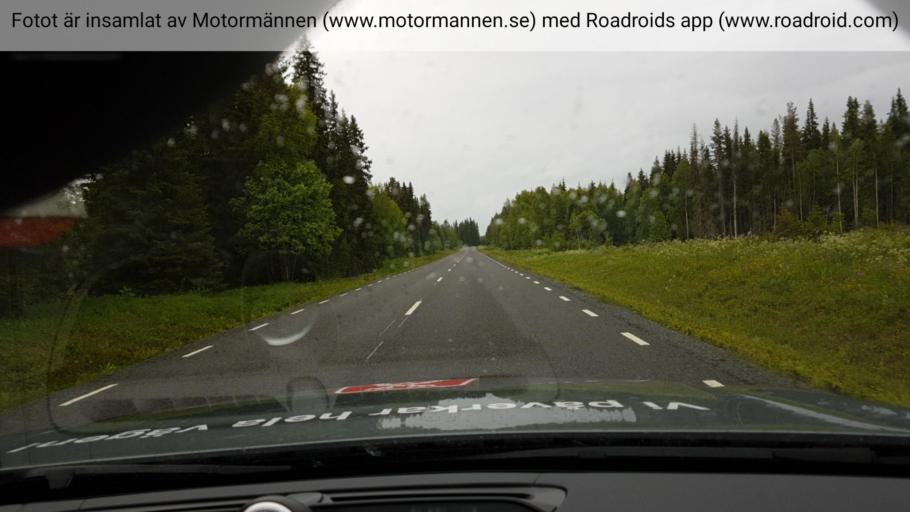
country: SE
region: Jaemtland
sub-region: Stroemsunds Kommun
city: Stroemsund
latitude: 63.6332
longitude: 15.1995
